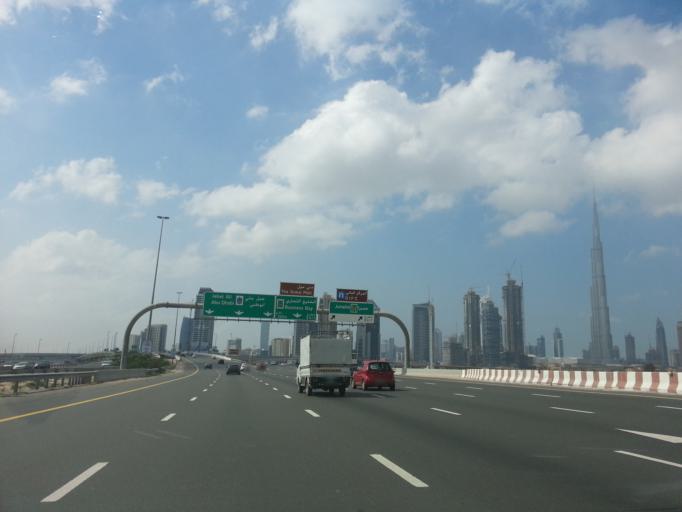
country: AE
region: Ash Shariqah
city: Sharjah
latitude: 25.1981
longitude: 55.2992
